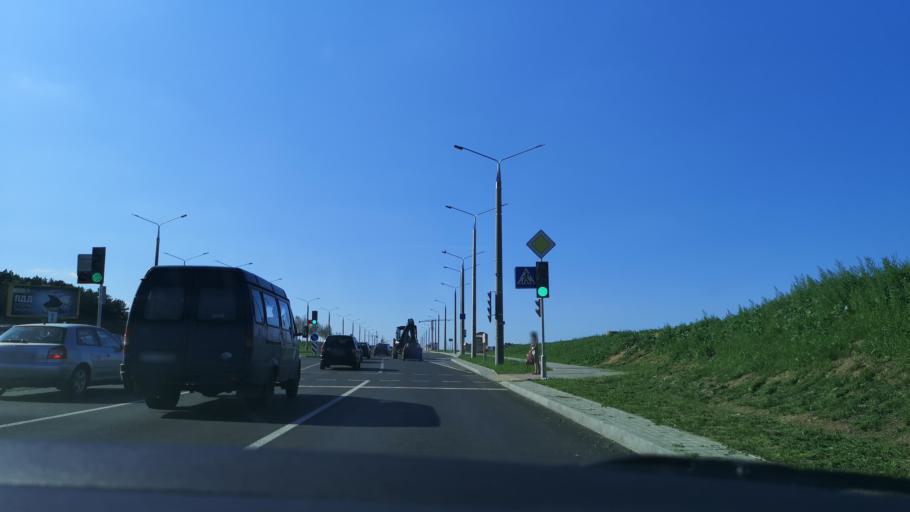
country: BY
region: Grodnenskaya
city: Hrodna
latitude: 53.6471
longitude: 23.8671
